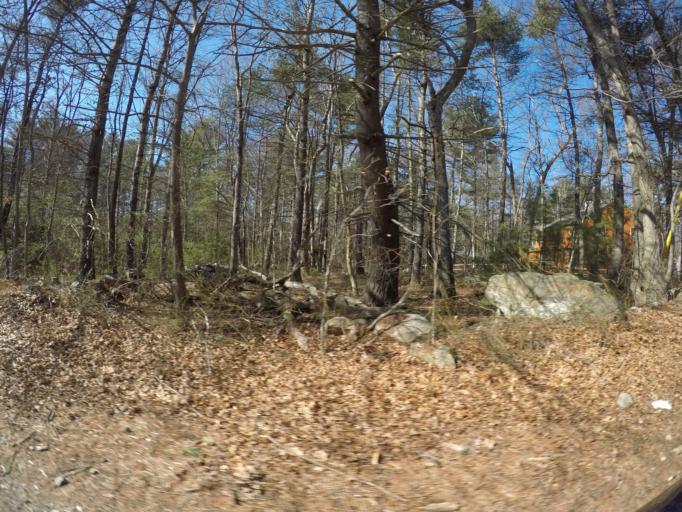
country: US
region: Massachusetts
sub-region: Bristol County
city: Easton
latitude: 42.0751
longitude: -71.1390
